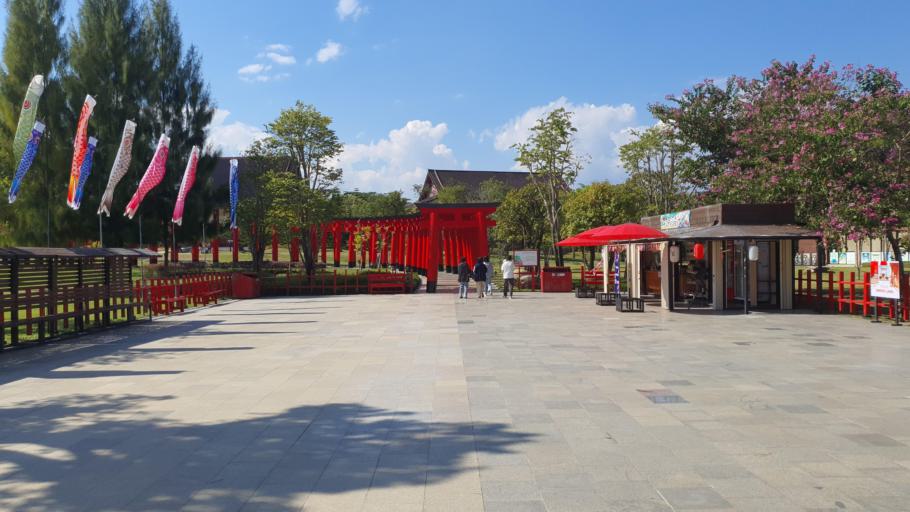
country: TH
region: Chiang Mai
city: Chai Prakan
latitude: 19.6560
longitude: 99.1490
